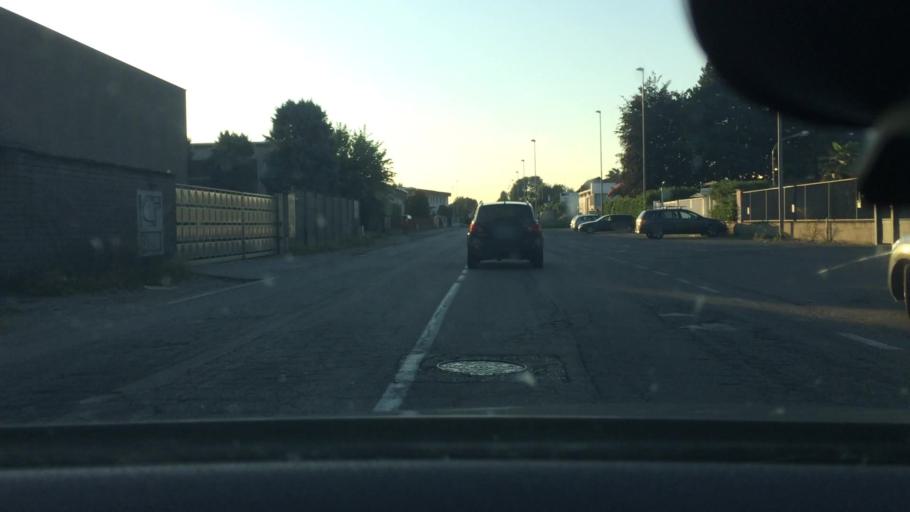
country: IT
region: Lombardy
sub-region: Citta metropolitana di Milano
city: Rescaldina
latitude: 45.6127
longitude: 8.9626
